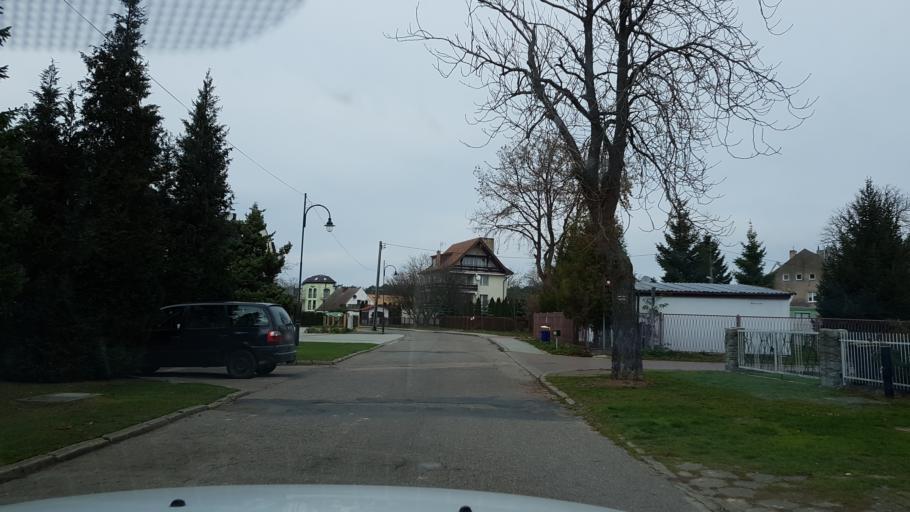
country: PL
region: West Pomeranian Voivodeship
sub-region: Powiat gryficki
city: Mrzezyno
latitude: 54.1424
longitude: 15.2908
